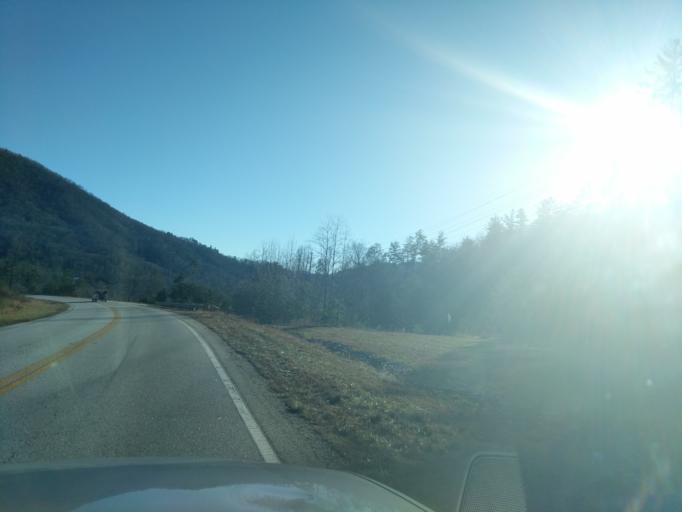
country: US
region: Georgia
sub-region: Rabun County
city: Clayton
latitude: 34.8646
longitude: -83.5188
